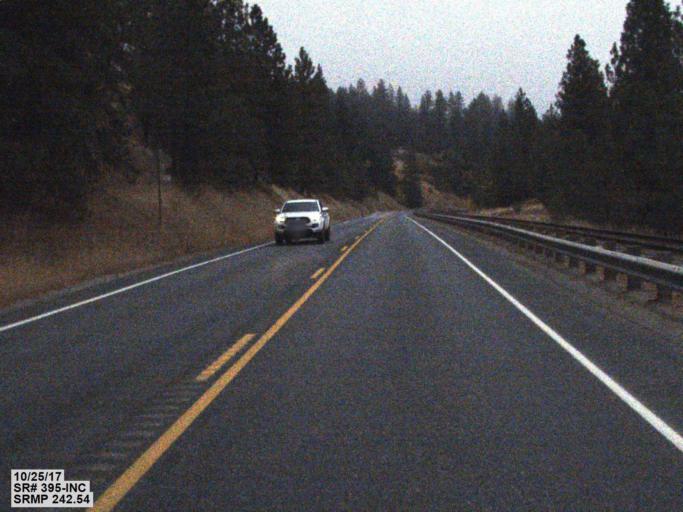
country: US
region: Washington
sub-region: Stevens County
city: Kettle Falls
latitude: 48.6364
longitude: -118.1193
